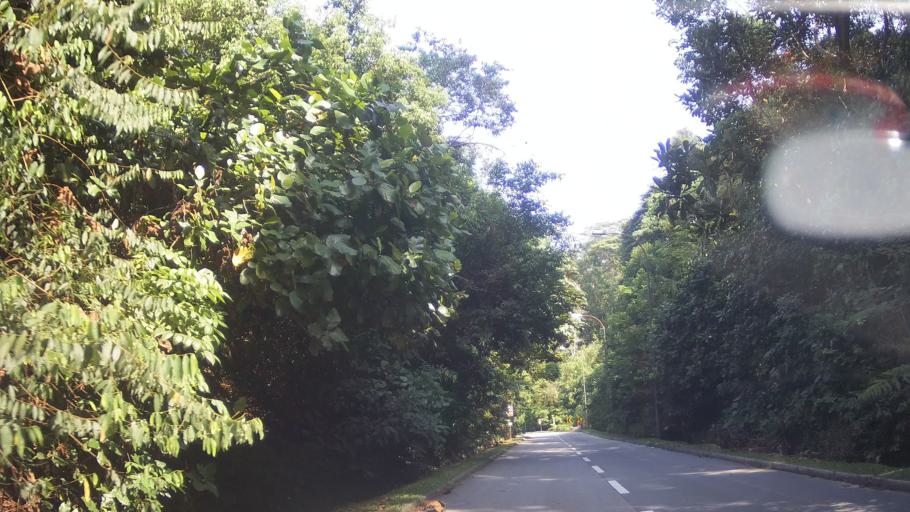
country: MY
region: Johor
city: Johor Bahru
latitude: 1.3716
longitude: 103.7788
